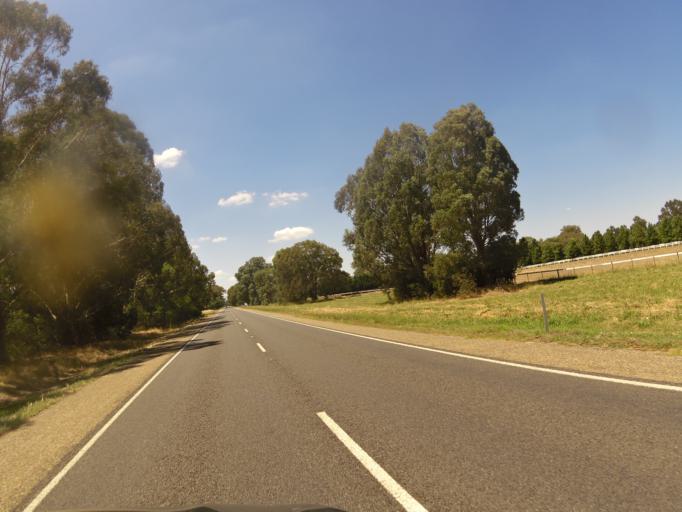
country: AU
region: Victoria
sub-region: Wangaratta
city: Wangaratta
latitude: -36.3867
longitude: 146.4273
